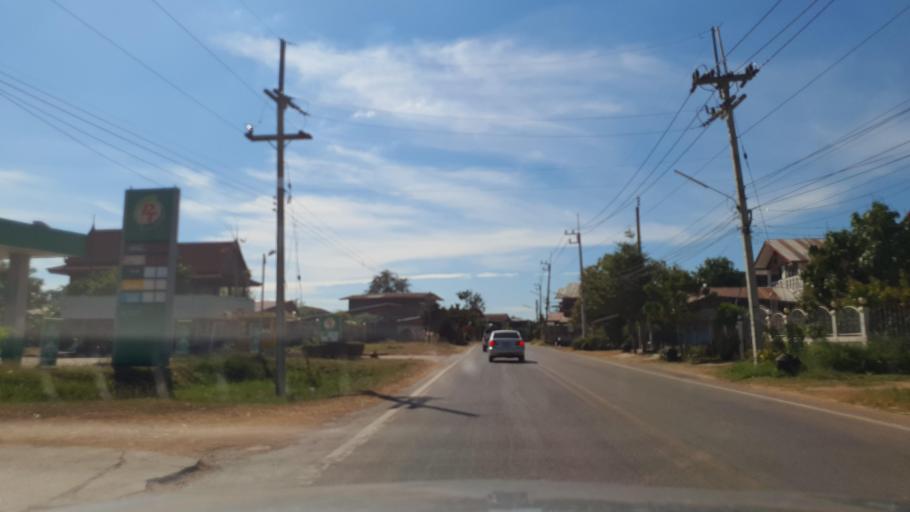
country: TH
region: Kalasin
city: Khao Wong
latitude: 16.7385
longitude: 104.1043
